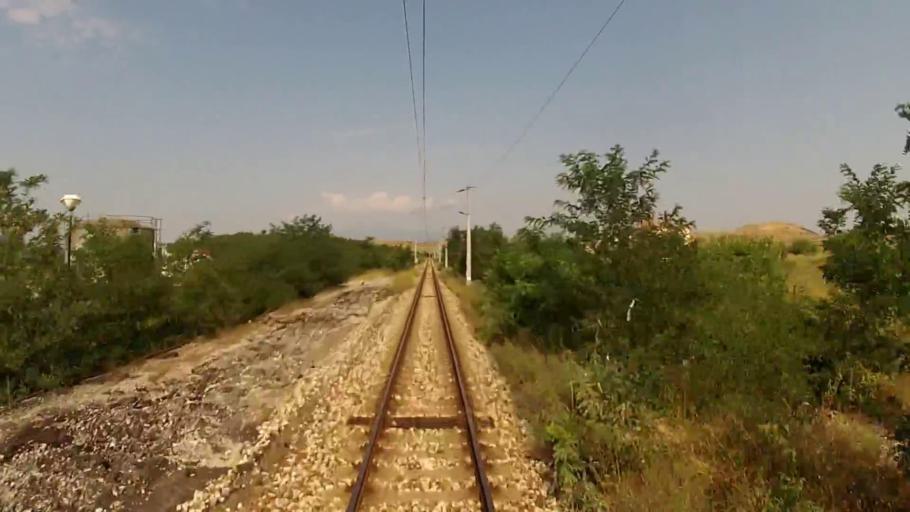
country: BG
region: Blagoevgrad
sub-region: Obshtina Petrich
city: Petrich
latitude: 41.4404
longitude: 23.3139
